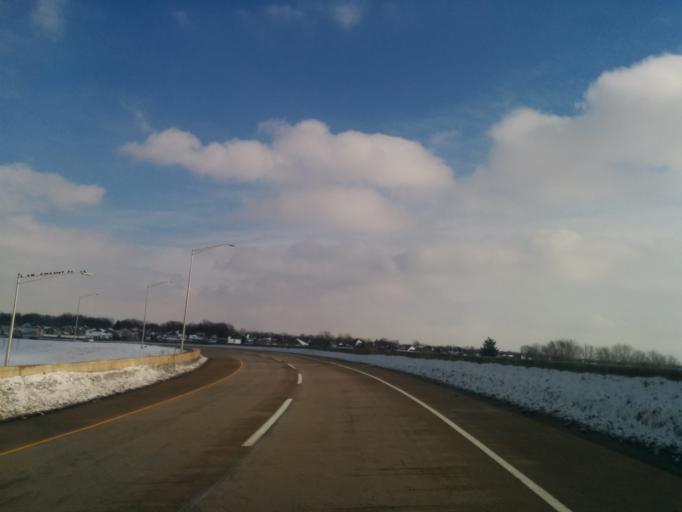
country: US
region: Illinois
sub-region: Will County
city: New Lenox
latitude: 41.5358
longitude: -87.9601
